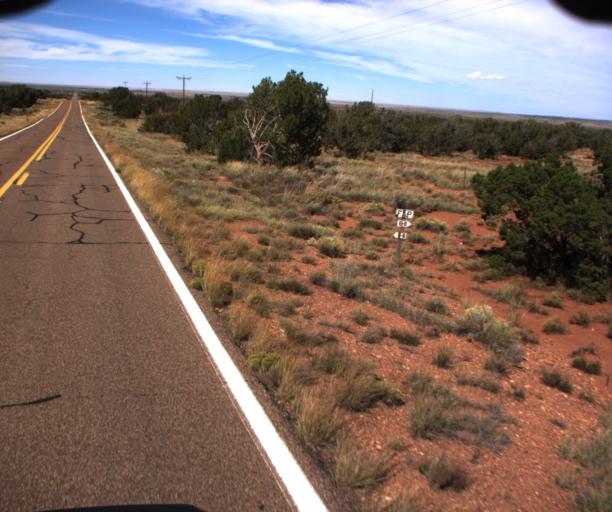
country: US
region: Arizona
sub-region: Apache County
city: Saint Johns
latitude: 34.5852
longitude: -109.6432
